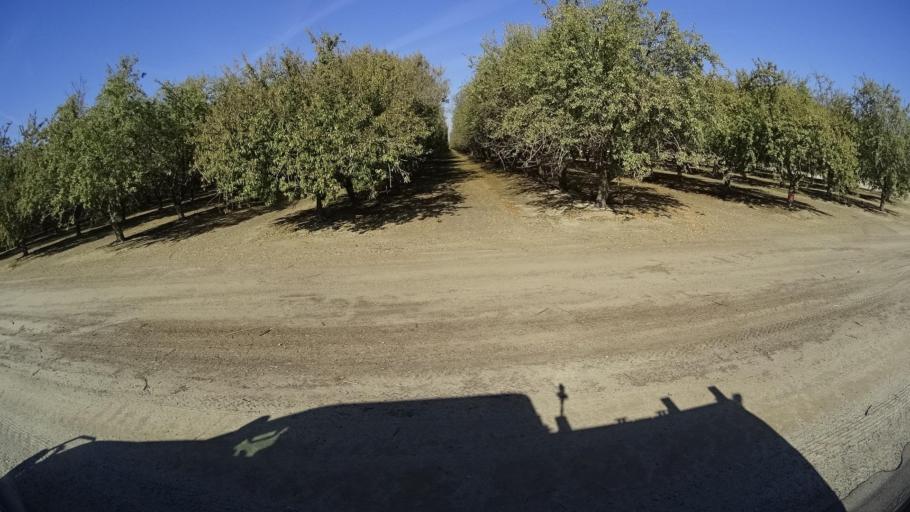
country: US
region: California
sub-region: Kern County
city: McFarland
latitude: 35.6466
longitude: -119.2687
